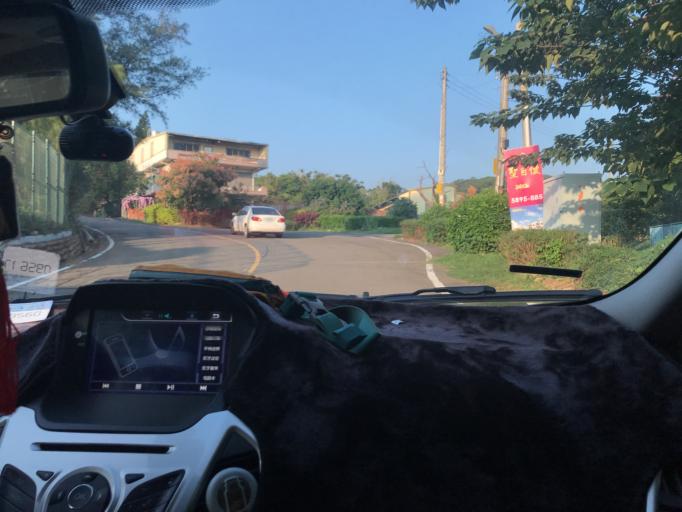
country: TW
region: Taiwan
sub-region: Hsinchu
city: Zhubei
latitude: 24.8437
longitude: 121.0370
